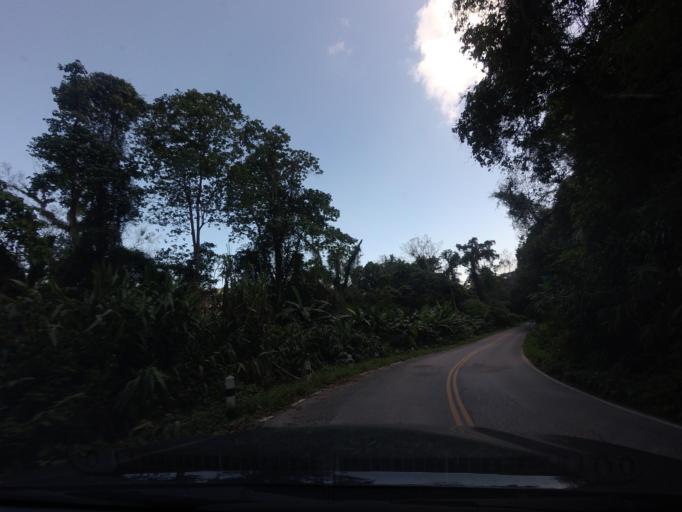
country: TH
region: Phetchabun
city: Lom Kao
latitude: 16.9156
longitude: 101.0743
